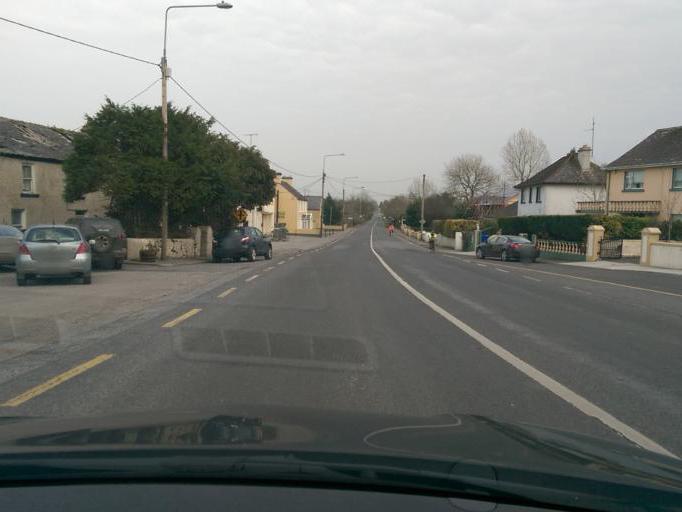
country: IE
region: Connaught
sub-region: Roscommon
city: Roscommon
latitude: 53.5236
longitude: -8.3218
